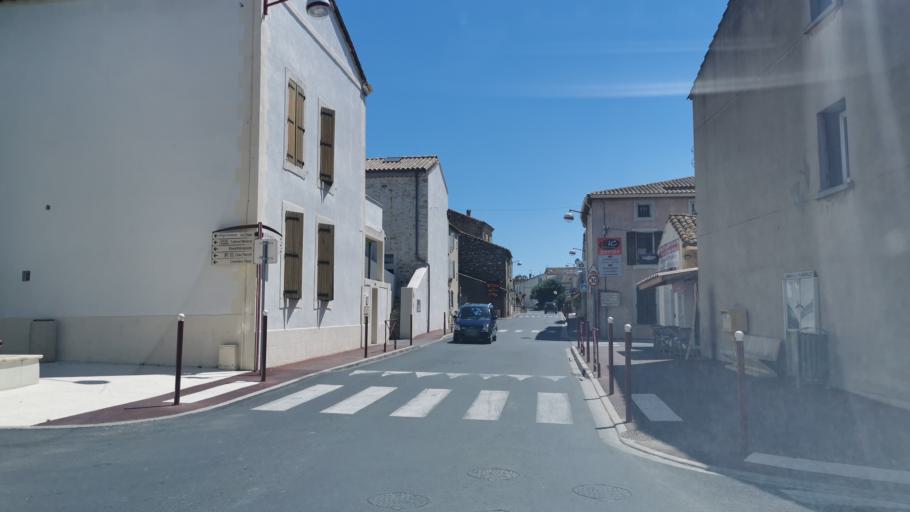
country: FR
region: Languedoc-Roussillon
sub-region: Departement de l'Aude
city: Vinassan
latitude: 43.2036
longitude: 3.0746
